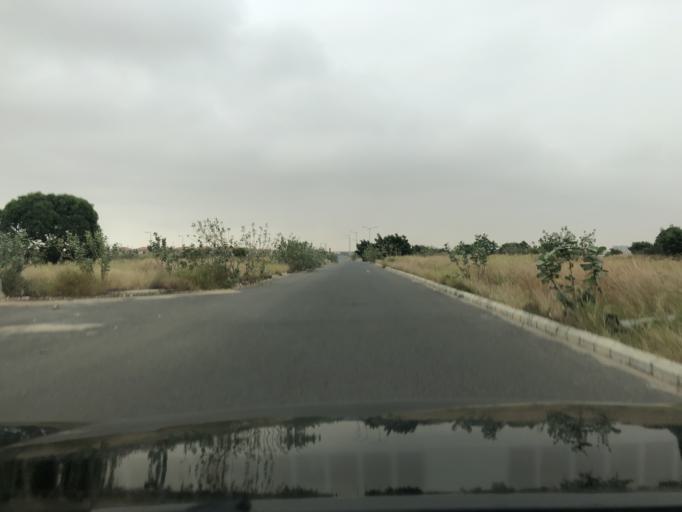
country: AO
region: Luanda
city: Luanda
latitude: -8.9523
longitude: 13.2494
